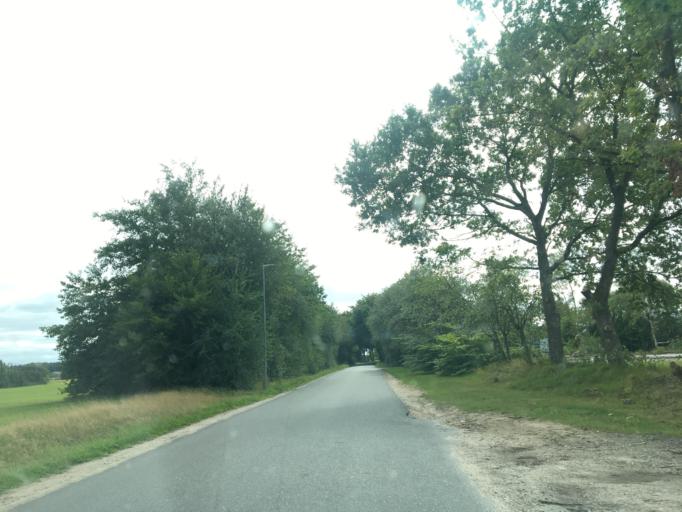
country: DK
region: North Denmark
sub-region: Vesthimmerland Kommune
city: Farso
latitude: 56.8766
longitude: 9.3997
